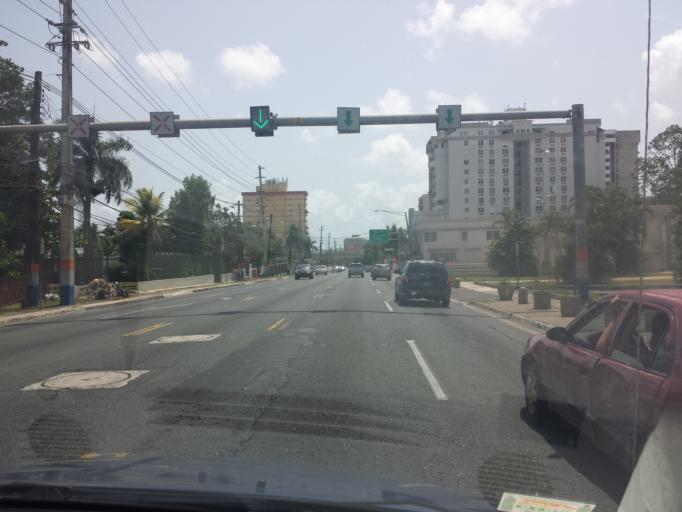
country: PR
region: Catano
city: Catano
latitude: 18.4050
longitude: -66.1135
